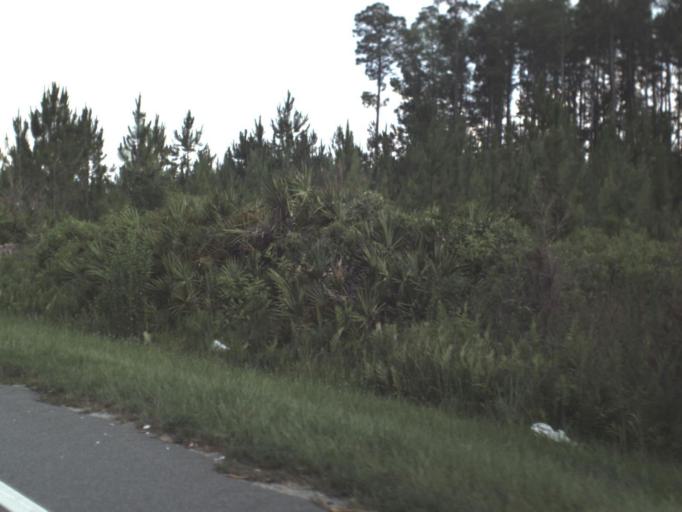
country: US
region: Florida
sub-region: Putnam County
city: Palatka
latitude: 29.6857
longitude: -81.7366
